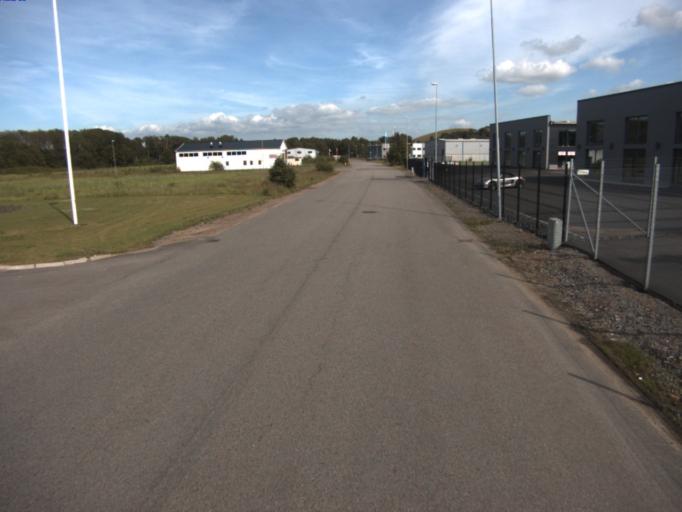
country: SE
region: Skane
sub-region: Helsingborg
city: Odakra
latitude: 56.0791
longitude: 12.7581
